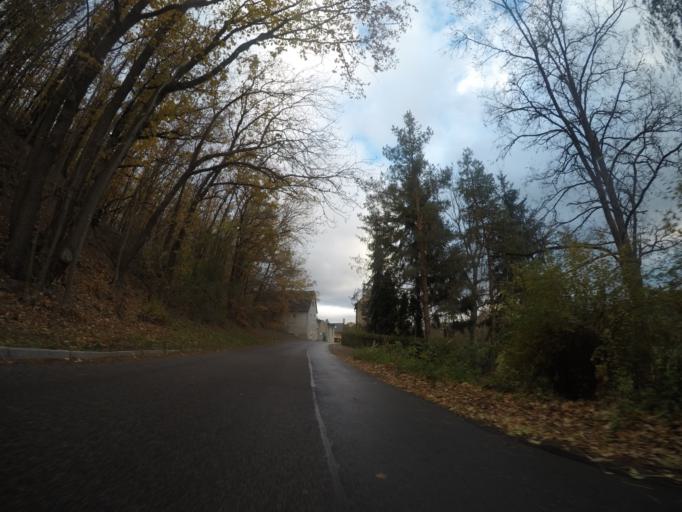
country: DE
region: Thuringia
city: Vollmershain
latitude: 50.8533
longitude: 12.2942
